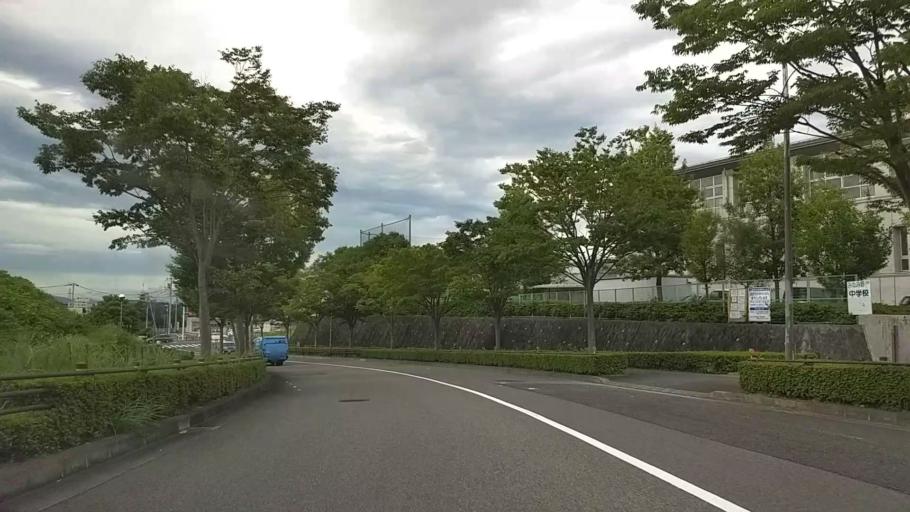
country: JP
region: Tokyo
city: Hachioji
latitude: 35.6316
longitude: 139.3209
